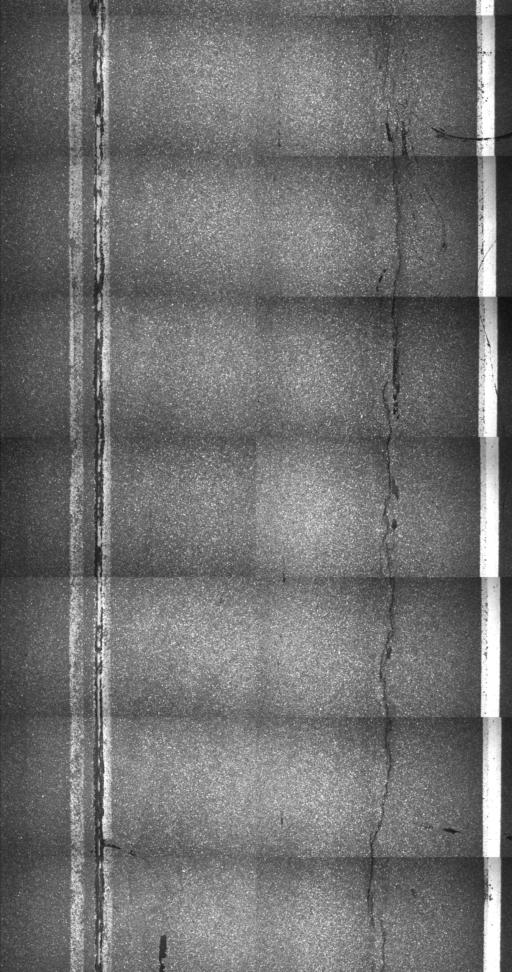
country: US
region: Vermont
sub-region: Addison County
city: Middlebury (village)
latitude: 43.9740
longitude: -73.0663
